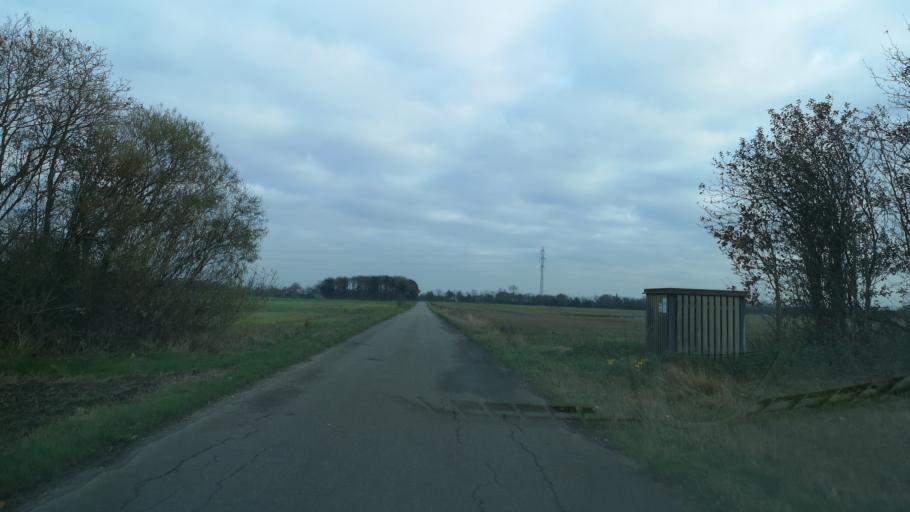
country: DK
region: Central Jutland
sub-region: Ringkobing-Skjern Kommune
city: Videbaek
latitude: 56.0355
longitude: 8.5858
